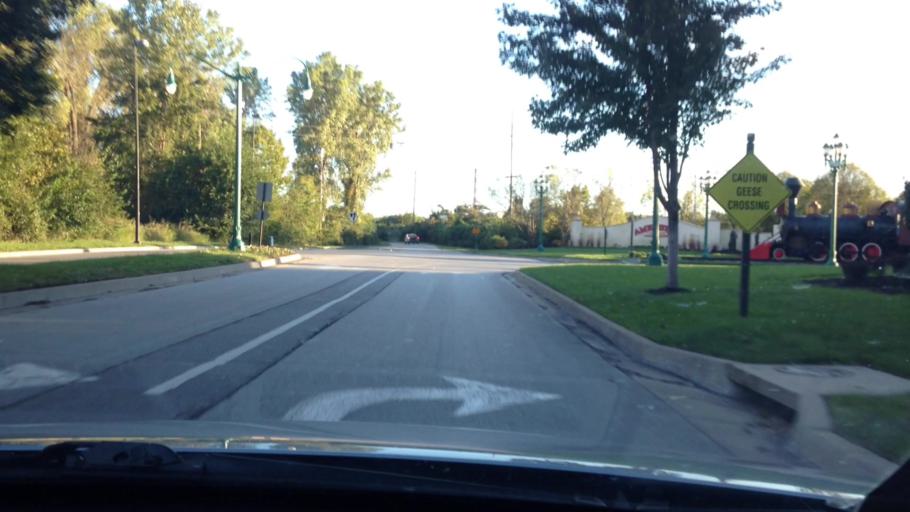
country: US
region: Missouri
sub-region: Clay County
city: Claycomo
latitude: 39.1524
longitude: -94.4773
